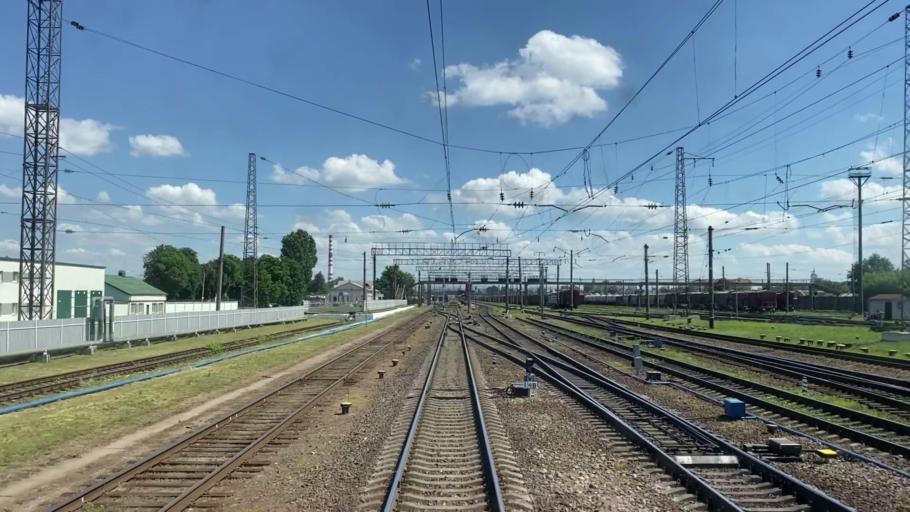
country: BY
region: Brest
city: Baranovichi
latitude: 53.1310
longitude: 25.9901
